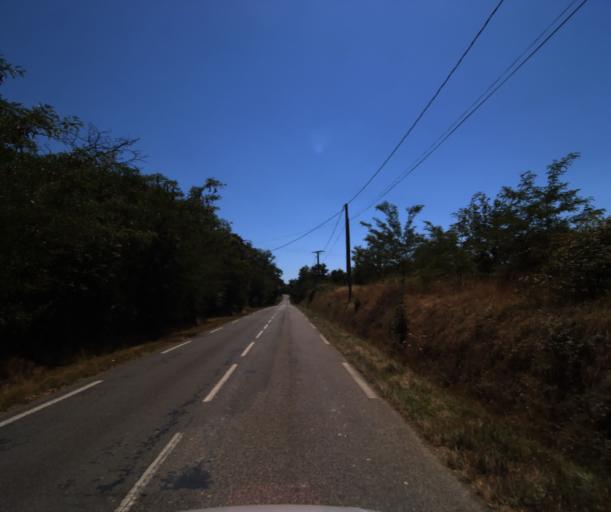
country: FR
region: Midi-Pyrenees
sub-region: Departement de la Haute-Garonne
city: Seysses
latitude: 43.4575
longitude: 1.2931
